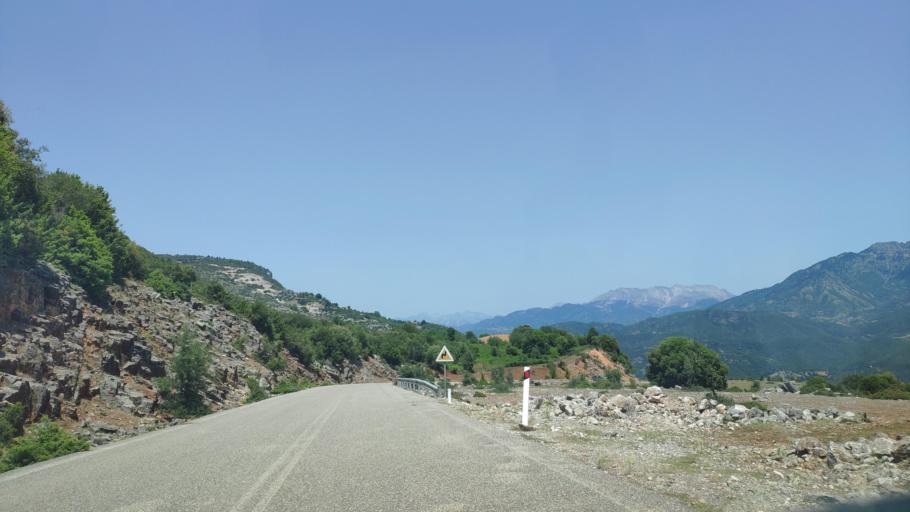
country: GR
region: Thessaly
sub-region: Nomos Kardhitsas
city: Anthiro
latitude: 39.1350
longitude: 21.3903
